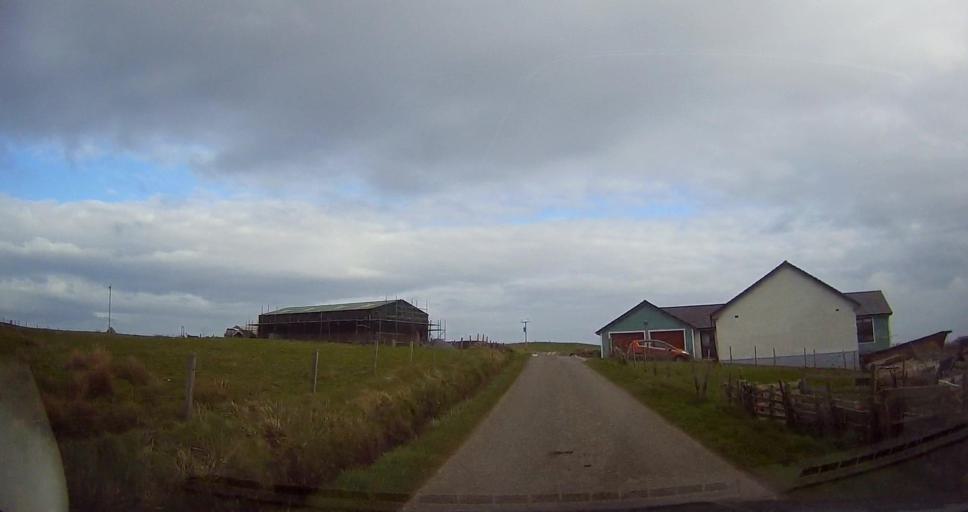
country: GB
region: Scotland
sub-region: Shetland Islands
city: Sandwick
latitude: 60.0437
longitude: -1.2050
